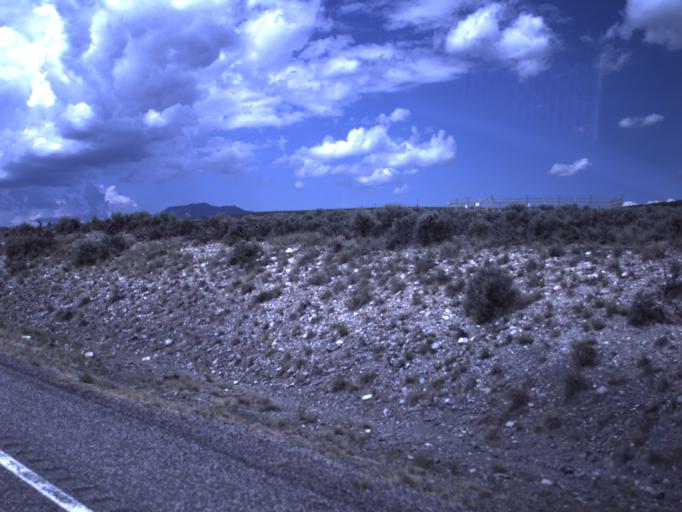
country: US
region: Utah
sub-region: Garfield County
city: Panguitch
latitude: 37.9927
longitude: -112.3912
